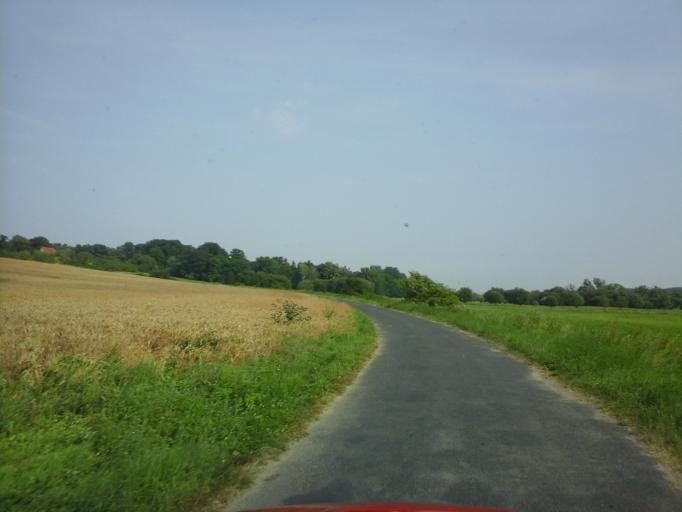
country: PL
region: West Pomeranian Voivodeship
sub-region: Powiat mysliborski
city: Barlinek
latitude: 53.0693
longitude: 15.2112
